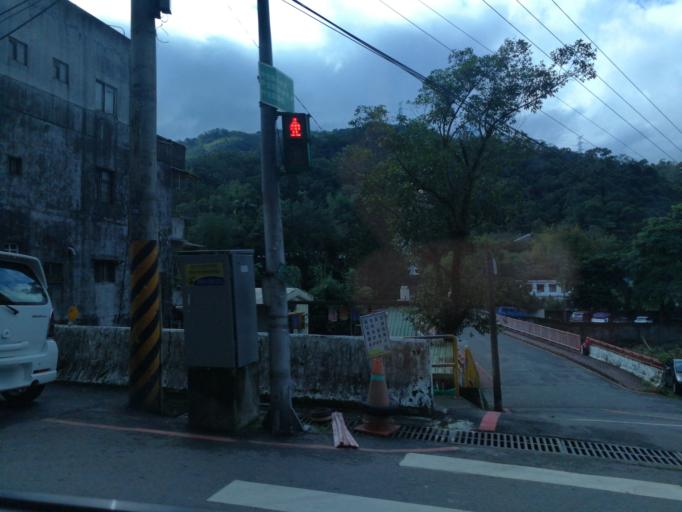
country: TW
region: Taipei
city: Taipei
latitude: 24.9539
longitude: 121.5624
